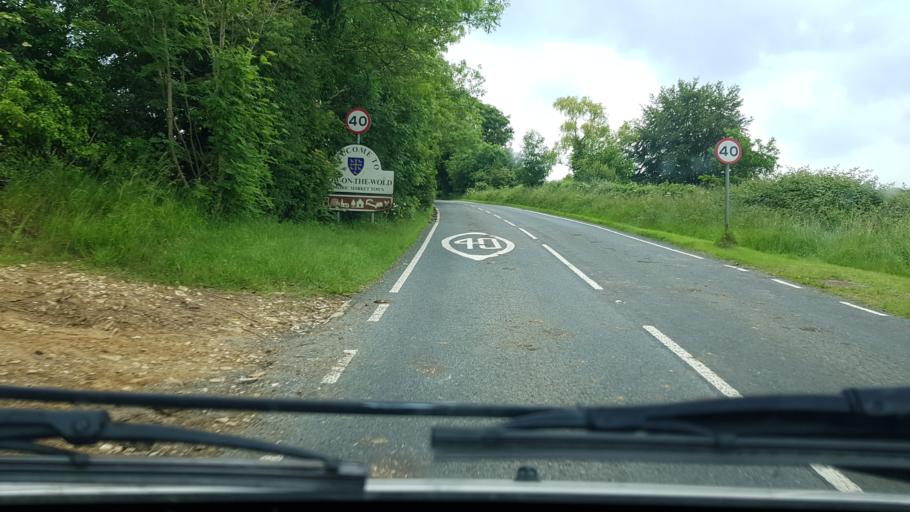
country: GB
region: England
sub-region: Gloucestershire
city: Stow on the Wold
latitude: 51.9375
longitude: -1.7278
